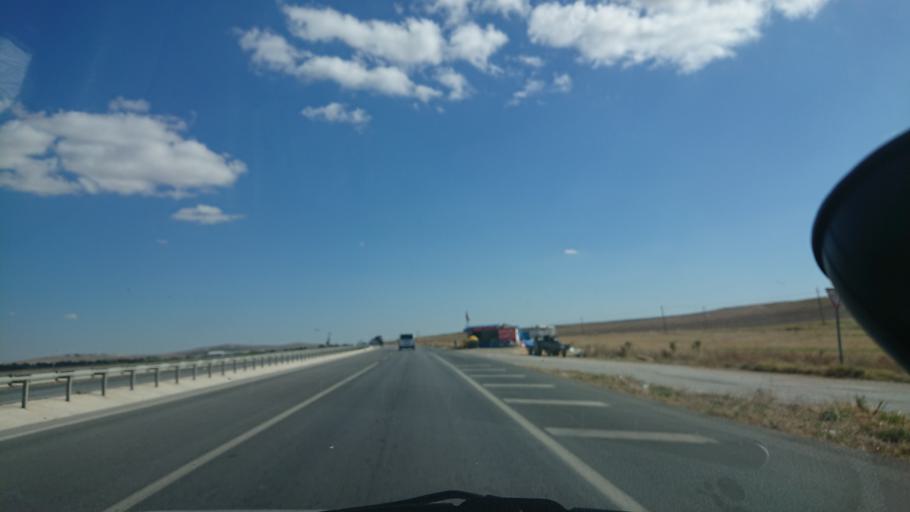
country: TR
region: Eskisehir
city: Mahmudiye
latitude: 39.5319
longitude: 30.9478
